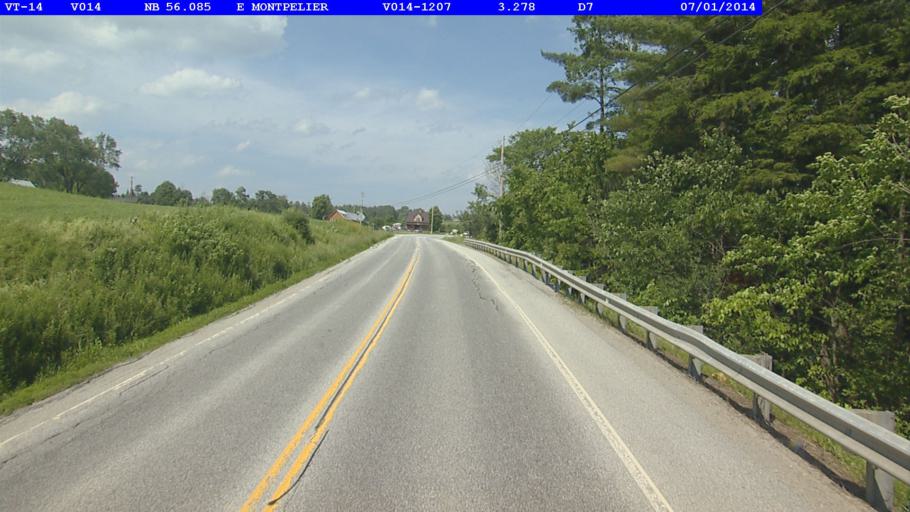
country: US
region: Vermont
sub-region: Washington County
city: Barre
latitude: 44.2792
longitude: -72.4747
